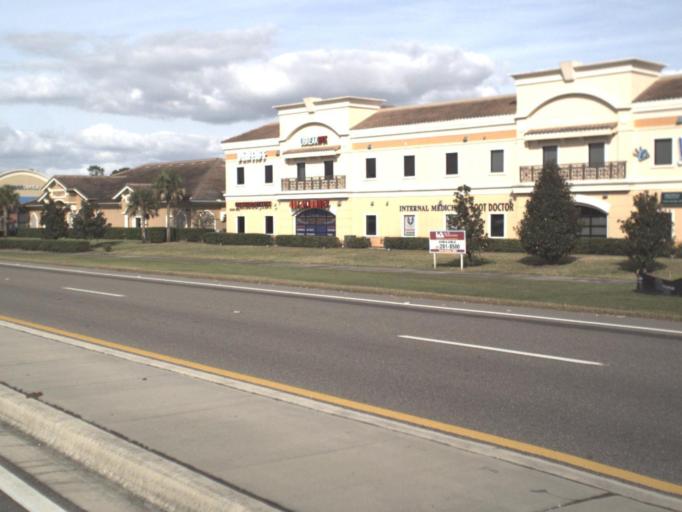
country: US
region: Florida
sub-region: Orange County
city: Hunters Creek
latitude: 28.3454
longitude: -81.4195
